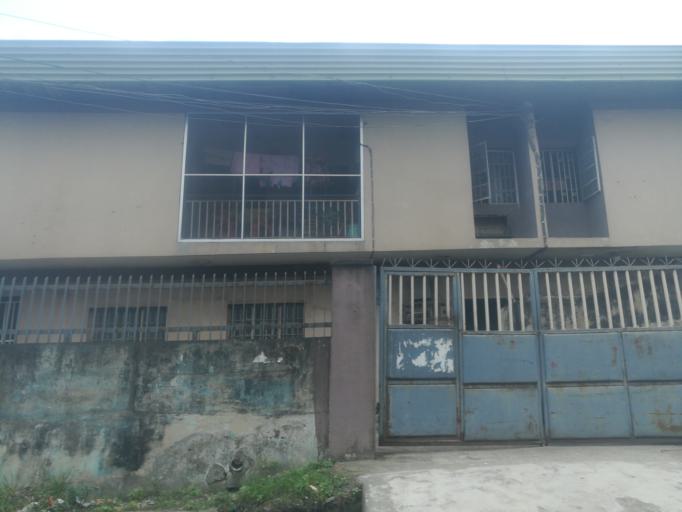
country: NG
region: Lagos
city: Ojota
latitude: 6.5606
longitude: 3.3928
